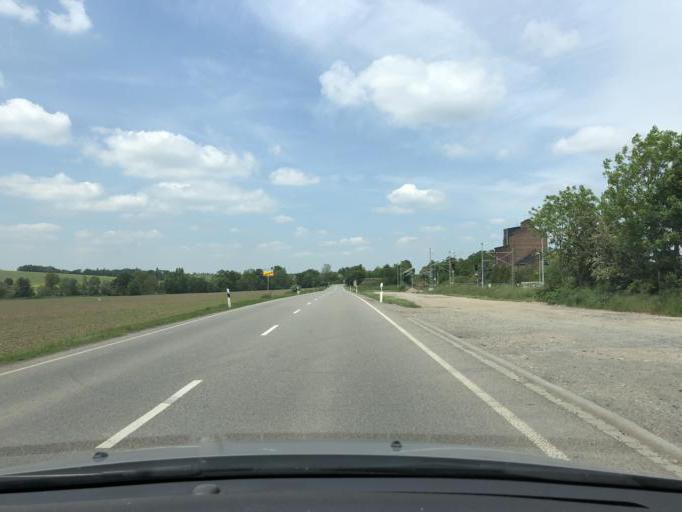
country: DE
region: Thuringia
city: Saara
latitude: 50.9383
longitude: 12.4252
